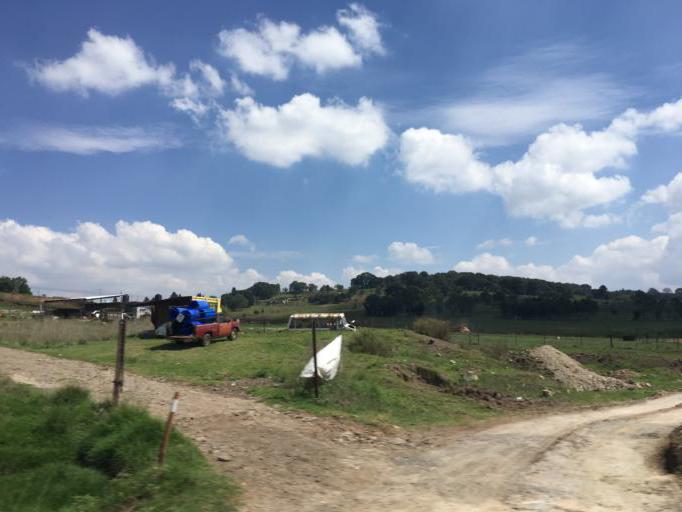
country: MX
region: Mexico
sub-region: Timilpan
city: Tercera Manzana de Zaragoza
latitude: 19.8847
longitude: -99.6525
